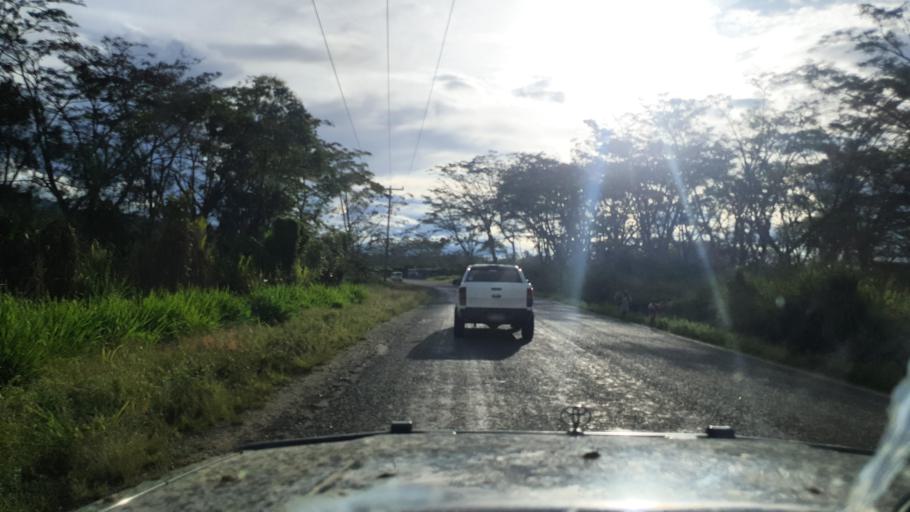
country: PG
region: Jiwaka
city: Minj
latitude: -5.8431
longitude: 144.6046
